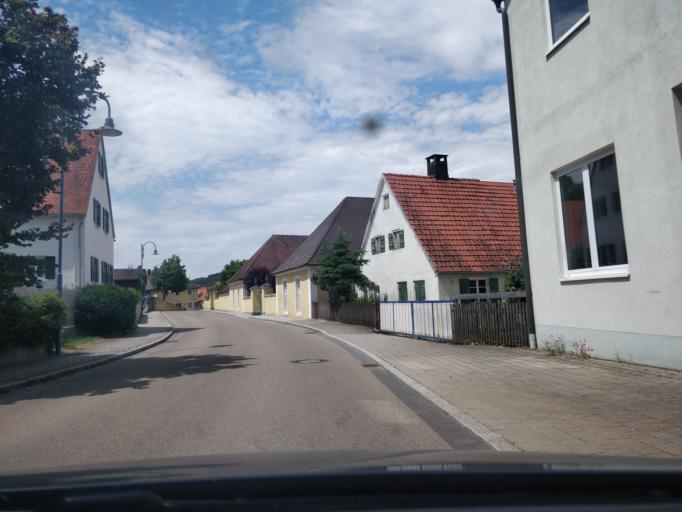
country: DE
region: Bavaria
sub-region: Swabia
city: Hohenaltheim
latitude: 48.7840
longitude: 10.5375
